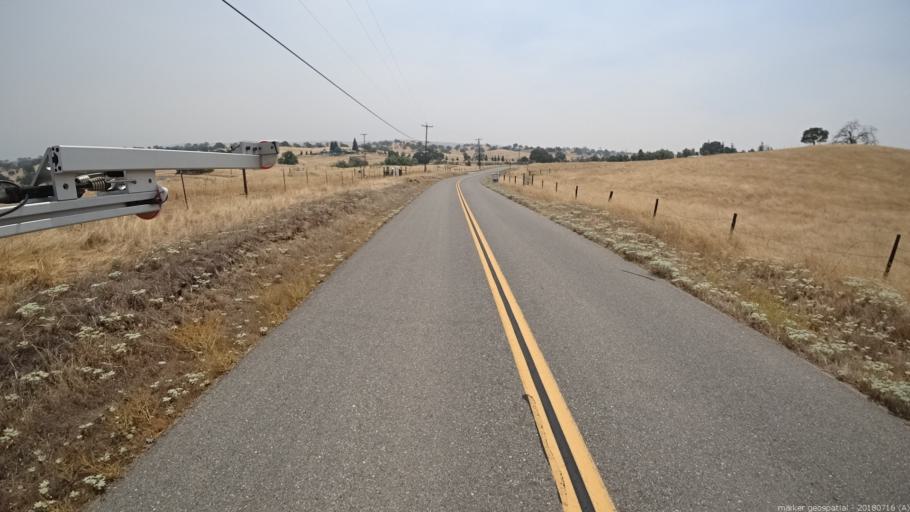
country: US
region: California
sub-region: Madera County
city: Yosemite Lakes
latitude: 37.1367
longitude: -119.9032
